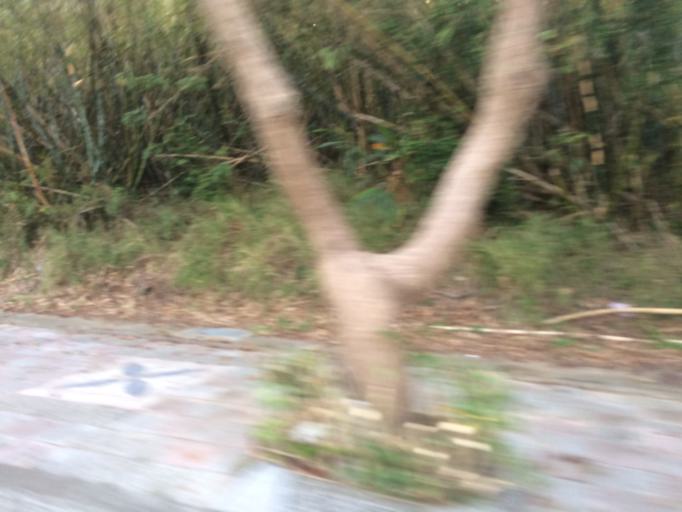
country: TW
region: Taiwan
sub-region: Hsinchu
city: Hsinchu
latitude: 24.7181
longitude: 120.9150
